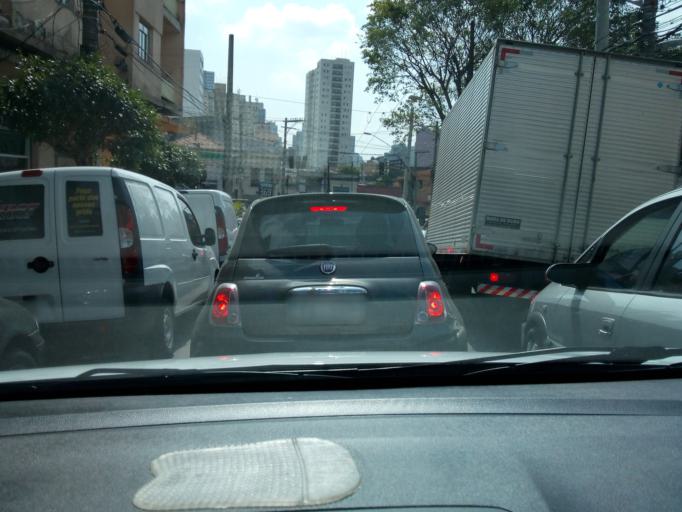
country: BR
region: Sao Paulo
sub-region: Sao Paulo
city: Sao Paulo
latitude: -23.5606
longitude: -46.6315
